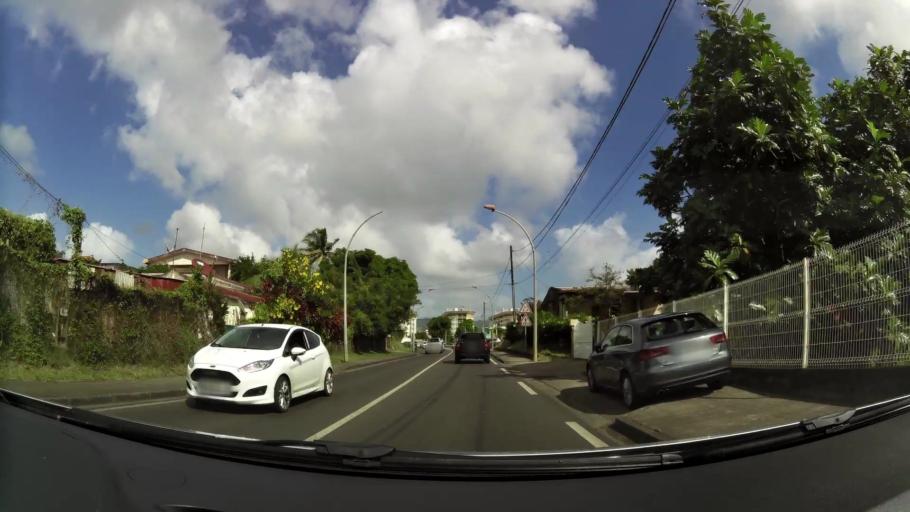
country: MQ
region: Martinique
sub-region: Martinique
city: Le Lamentin
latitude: 14.6106
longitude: -61.0023
